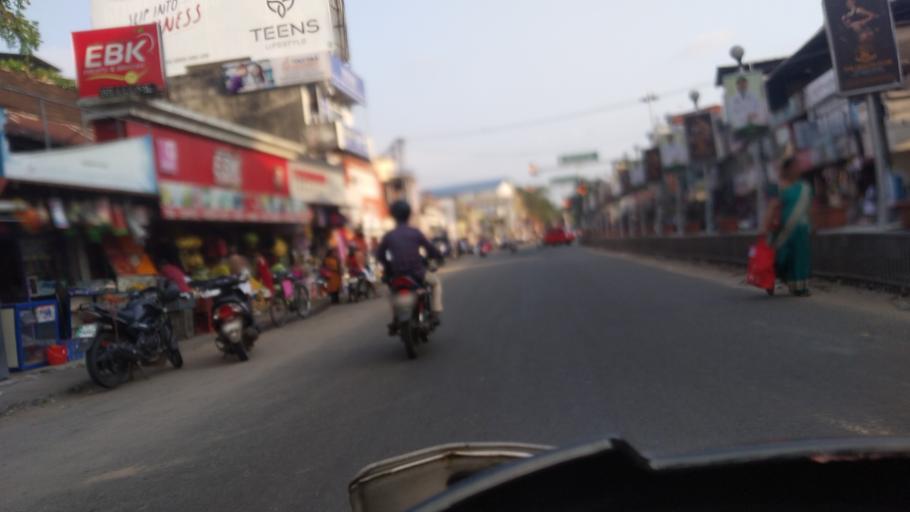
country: IN
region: Kerala
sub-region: Thrissur District
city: Thanniyam
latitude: 10.4135
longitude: 76.1079
